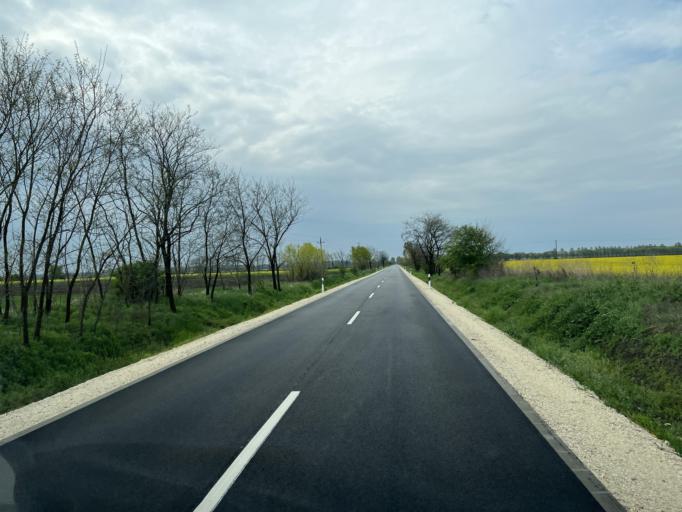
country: HU
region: Pest
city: Nyaregyhaza
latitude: 47.2476
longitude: 19.5212
